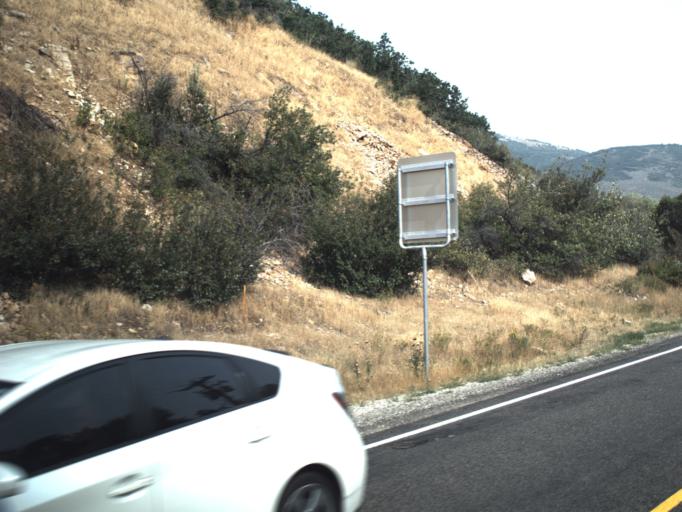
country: US
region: Utah
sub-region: Summit County
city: Kamas
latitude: 40.6423
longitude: -111.2713
